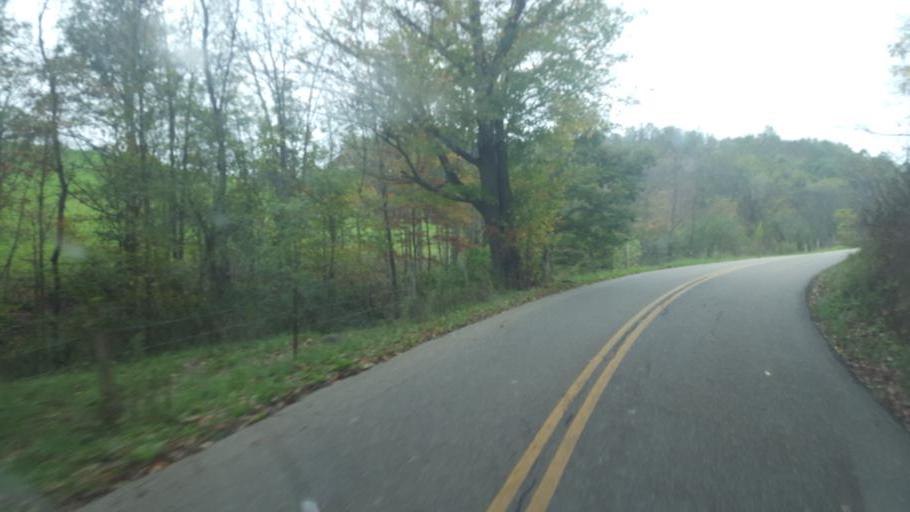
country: US
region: Ohio
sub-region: Carroll County
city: Carrollton
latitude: 40.4660
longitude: -81.0349
